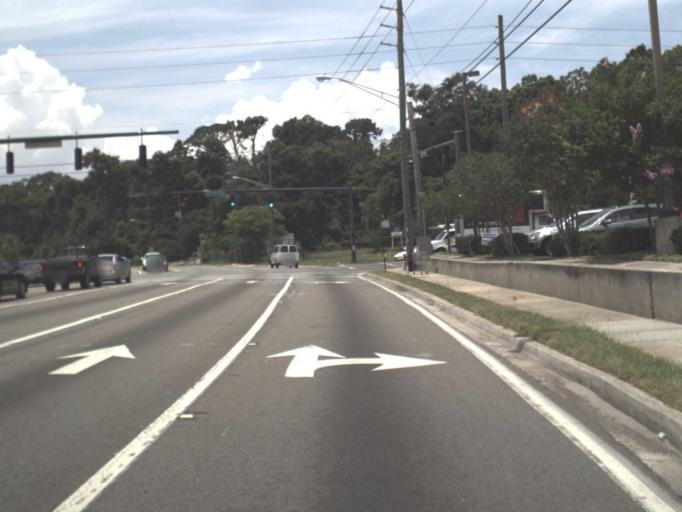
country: US
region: Florida
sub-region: Duval County
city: Jacksonville
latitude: 30.3139
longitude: -81.5987
